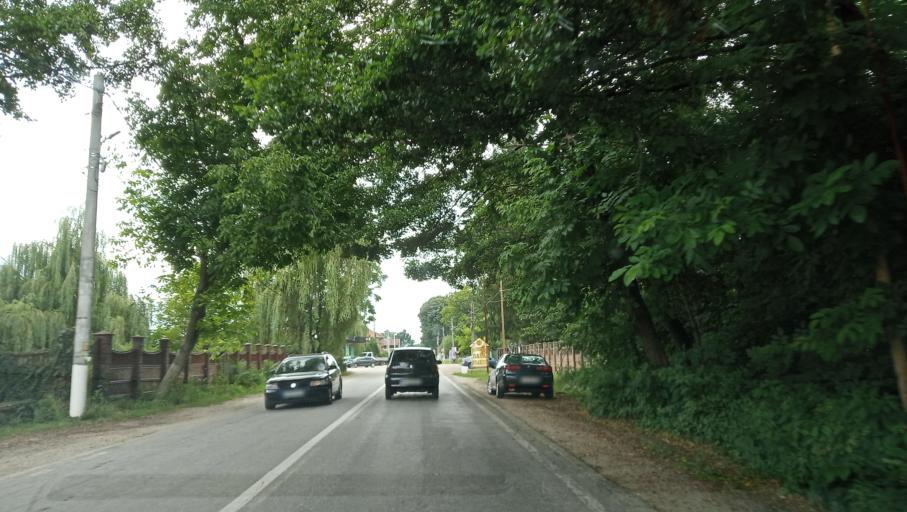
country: RO
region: Gorj
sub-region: Comuna Pestisani
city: Pestisani
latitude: 45.0812
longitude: 23.0563
